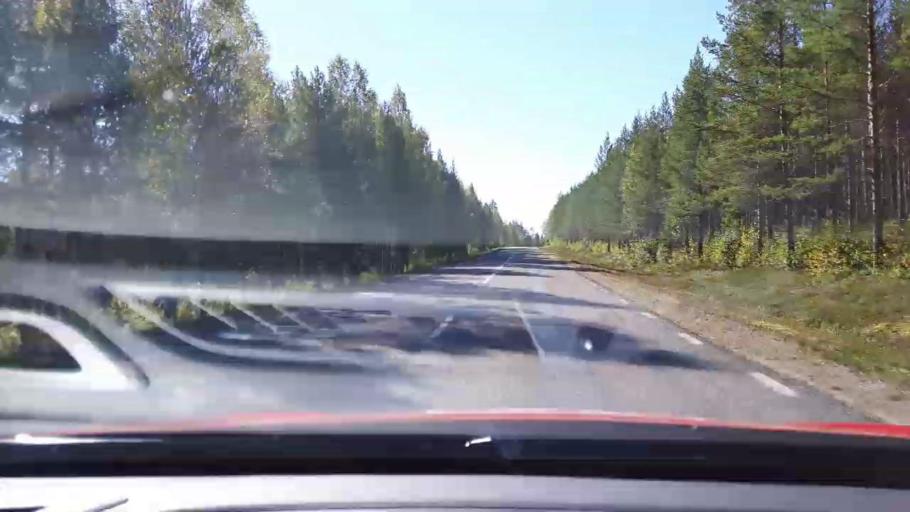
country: SE
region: Jaemtland
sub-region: Harjedalens Kommun
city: Sveg
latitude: 62.1316
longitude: 14.1670
